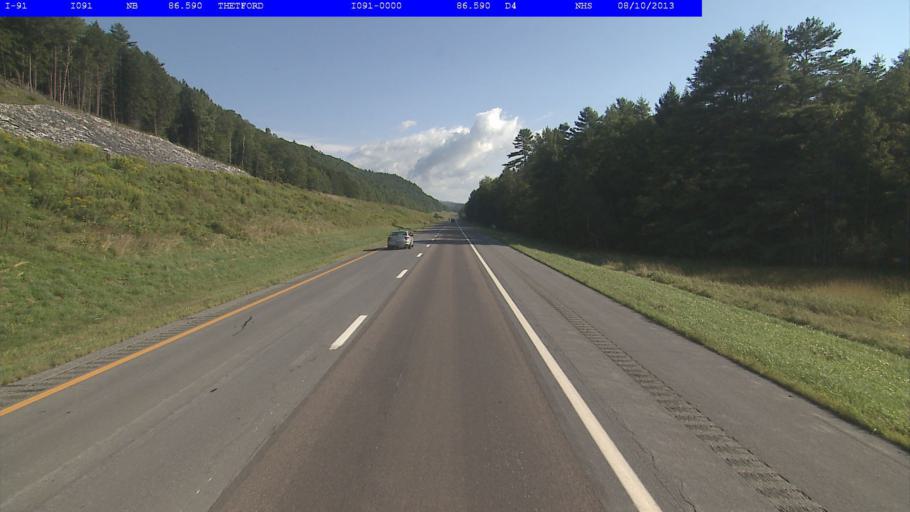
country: US
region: New Hampshire
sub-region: Grafton County
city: Lyme
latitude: 43.8445
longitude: -72.1992
